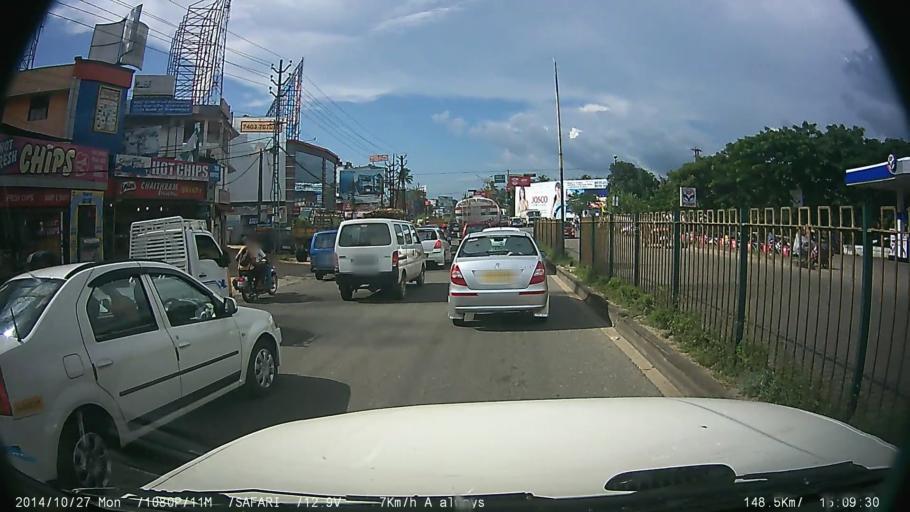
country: IN
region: Kerala
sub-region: Ernakulam
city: Aluva
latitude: 10.1189
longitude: 76.3433
